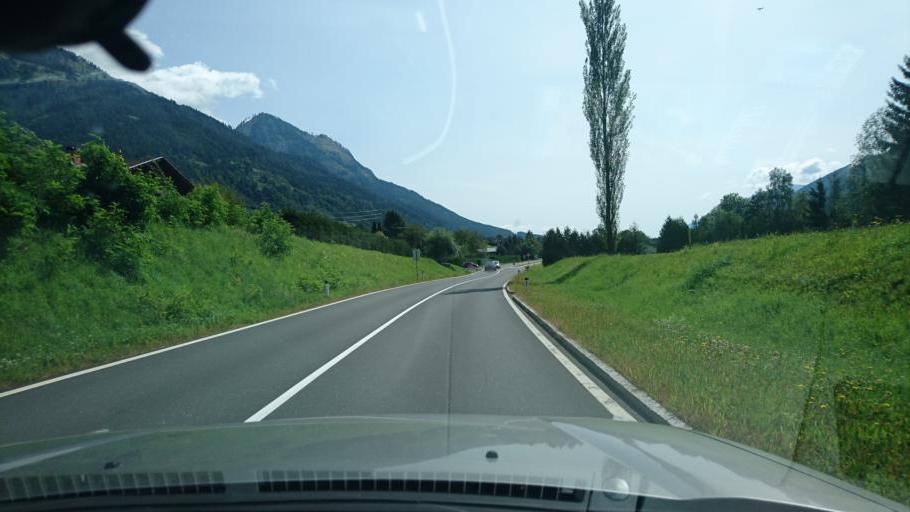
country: AT
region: Carinthia
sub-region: Politischer Bezirk Spittal an der Drau
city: Muhldorf
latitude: 46.8760
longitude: 13.3060
